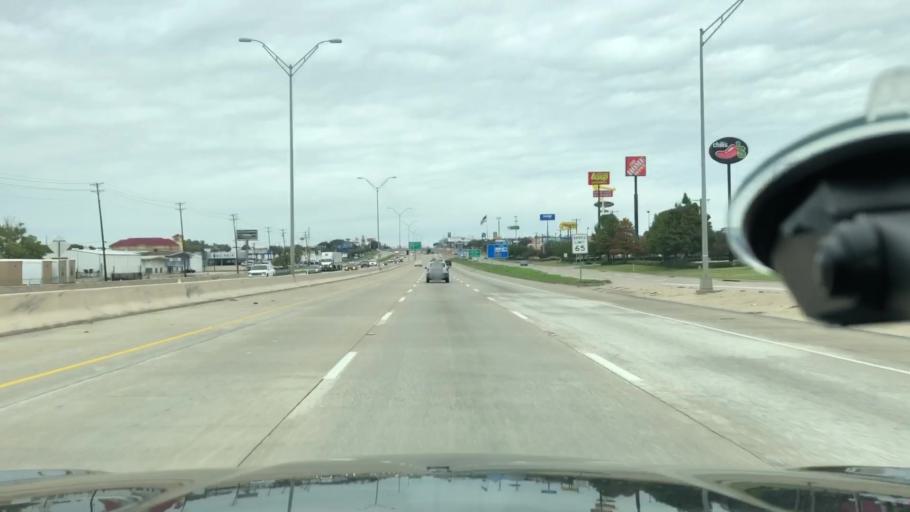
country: US
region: Texas
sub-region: Dallas County
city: DeSoto
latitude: 32.5940
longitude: -96.8224
